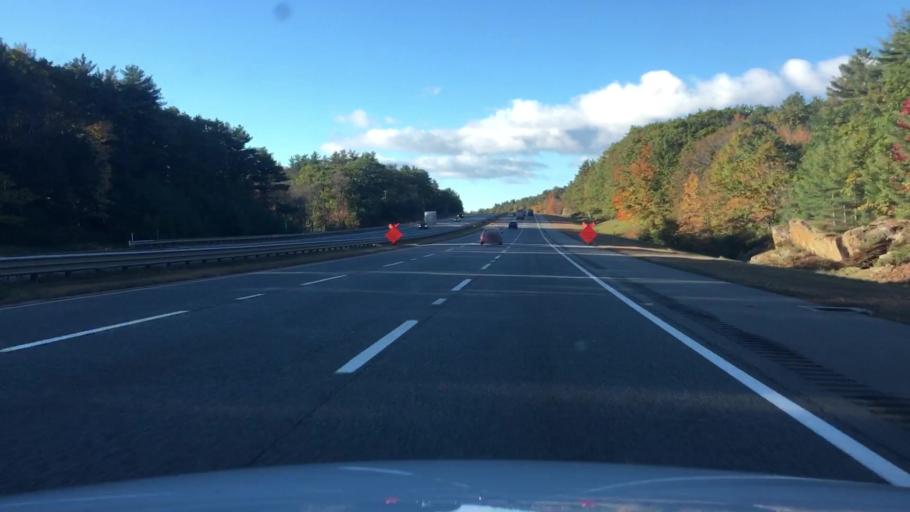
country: US
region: Maine
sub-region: York County
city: Ogunquit
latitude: 43.2386
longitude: -70.6314
